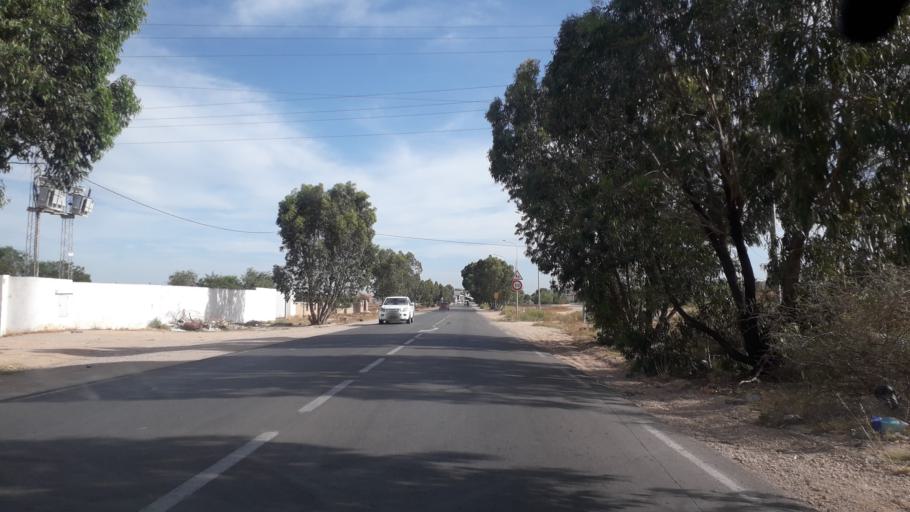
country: TN
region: Safaqis
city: Al Qarmadah
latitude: 34.8895
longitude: 10.7627
